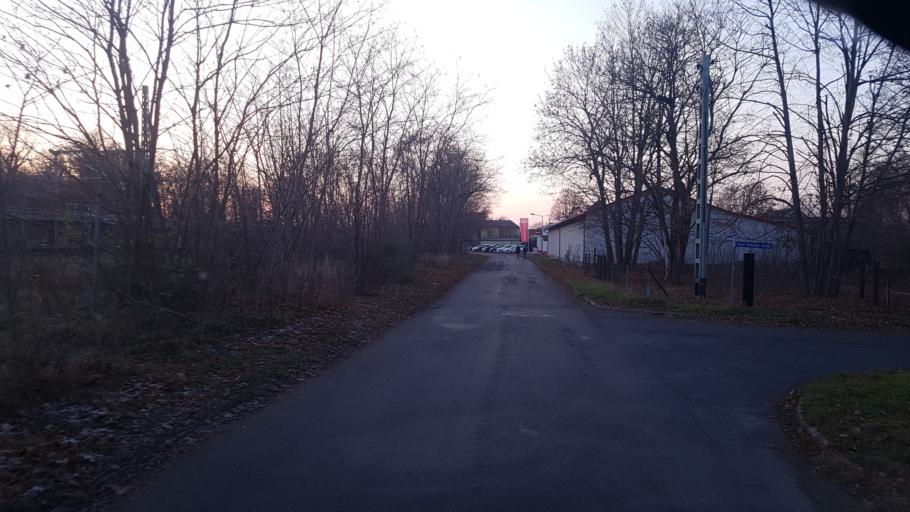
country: DE
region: Brandenburg
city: Lauchhammer
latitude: 51.4750
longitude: 13.7407
